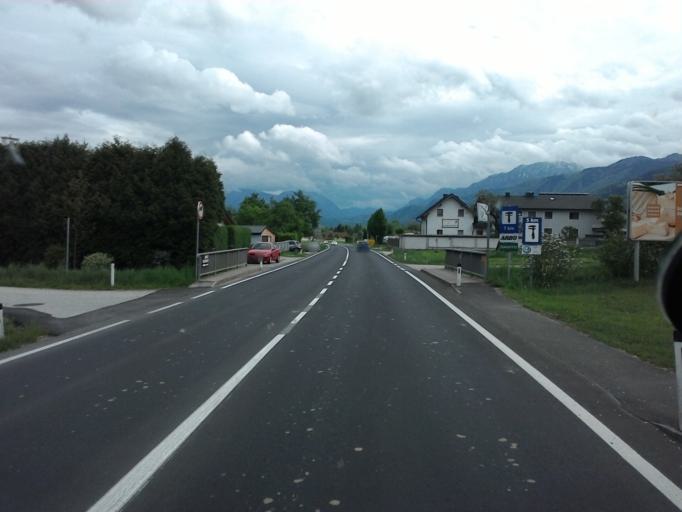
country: AT
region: Upper Austria
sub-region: Politischer Bezirk Kirchdorf an der Krems
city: Micheldorf in Oberoesterreich
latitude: 47.9287
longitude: 14.0872
